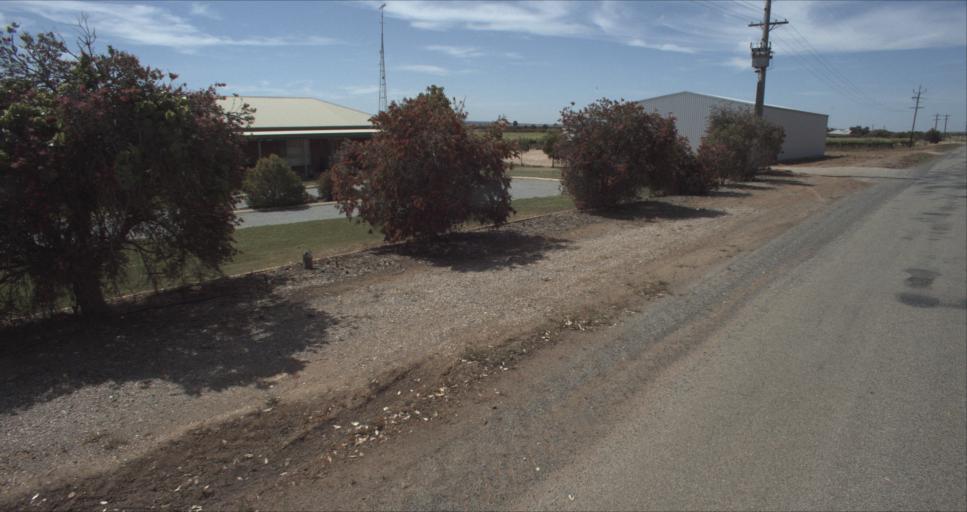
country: AU
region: New South Wales
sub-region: Leeton
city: Leeton
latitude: -34.5633
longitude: 146.4614
